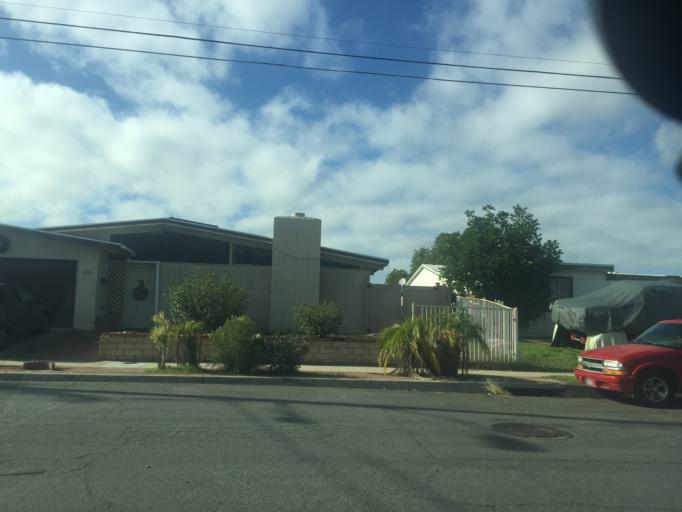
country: US
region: California
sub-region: San Diego County
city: San Diego
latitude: 32.7855
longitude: -117.1513
